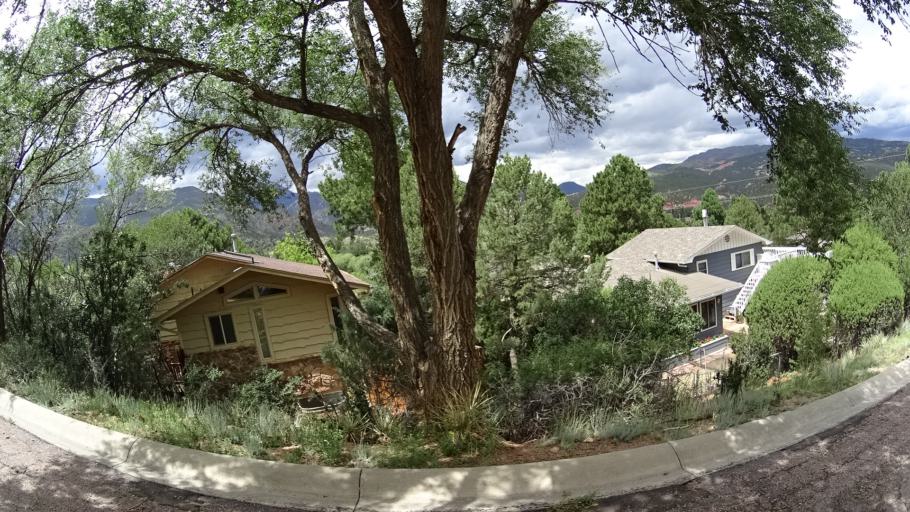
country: US
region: Colorado
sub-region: El Paso County
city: Manitou Springs
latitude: 38.8530
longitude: -104.8928
